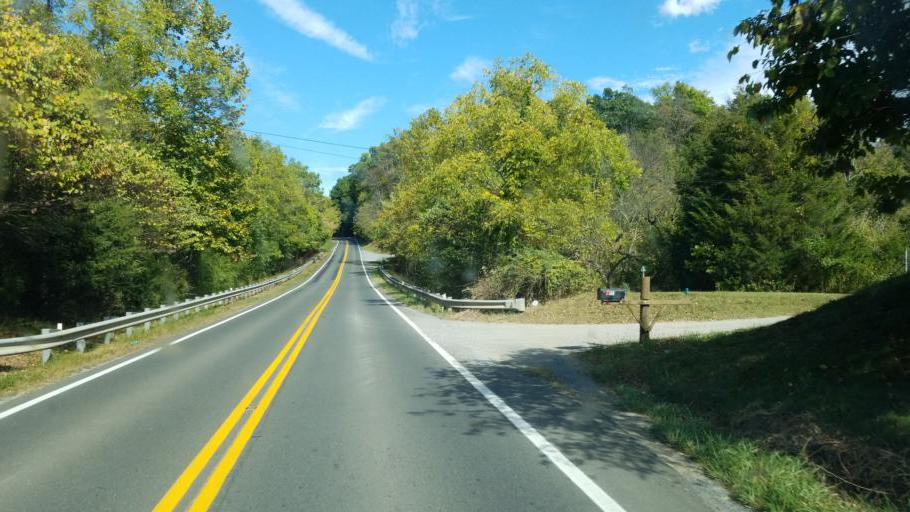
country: US
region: Virginia
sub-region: Warren County
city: Front Royal
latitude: 38.8637
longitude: -78.2574
